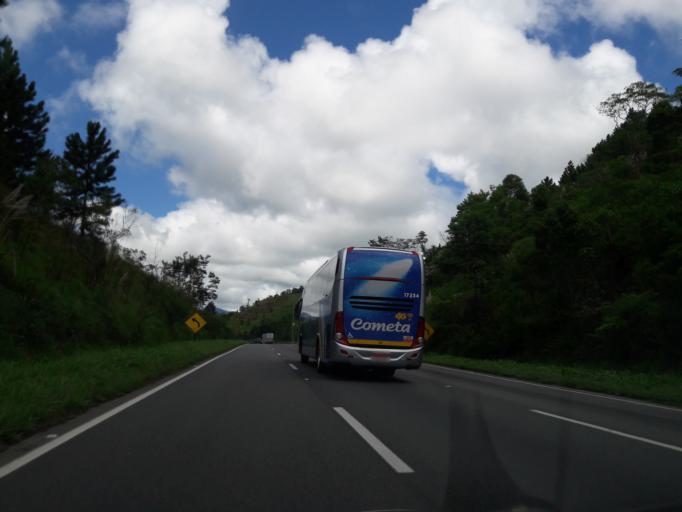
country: BR
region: Sao Paulo
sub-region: Cajati
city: Cajati
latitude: -24.9834
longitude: -48.5069
